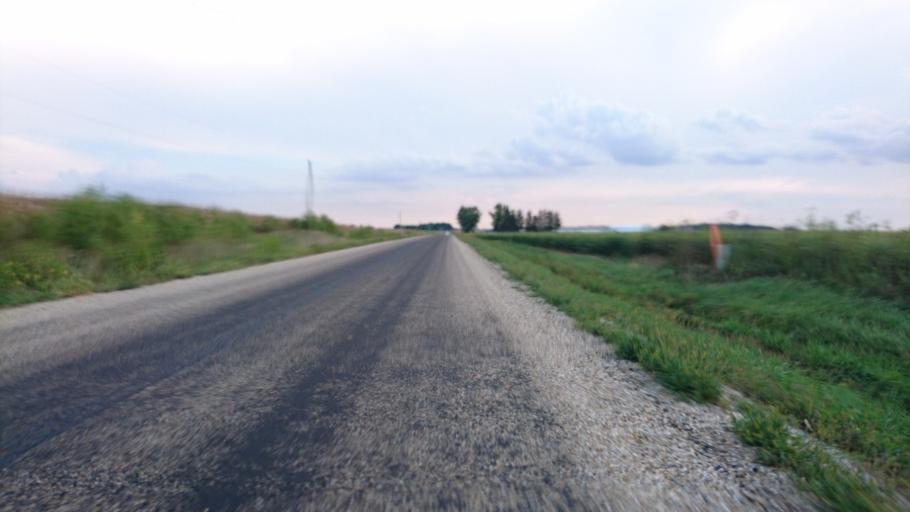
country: US
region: Illinois
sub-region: Logan County
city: Atlanta
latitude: 40.2410
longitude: -89.2049
